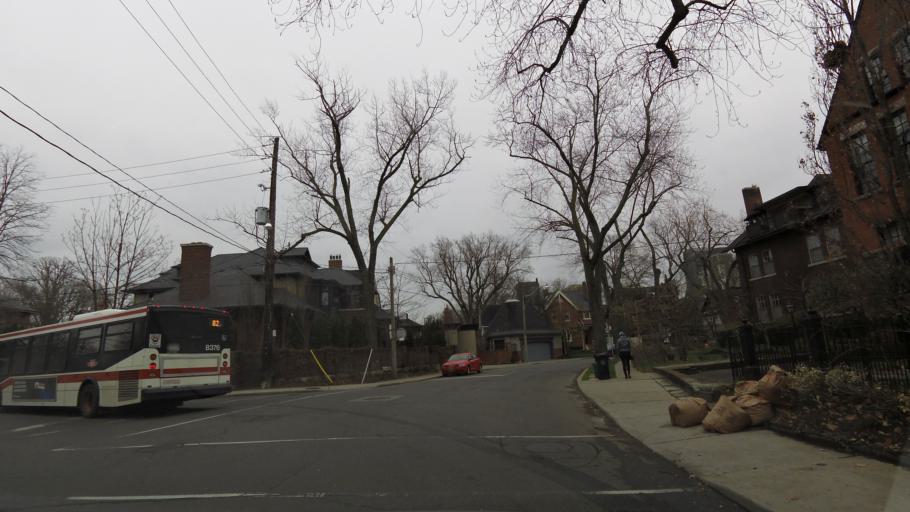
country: CA
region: Ontario
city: Toronto
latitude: 43.6775
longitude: -79.3777
